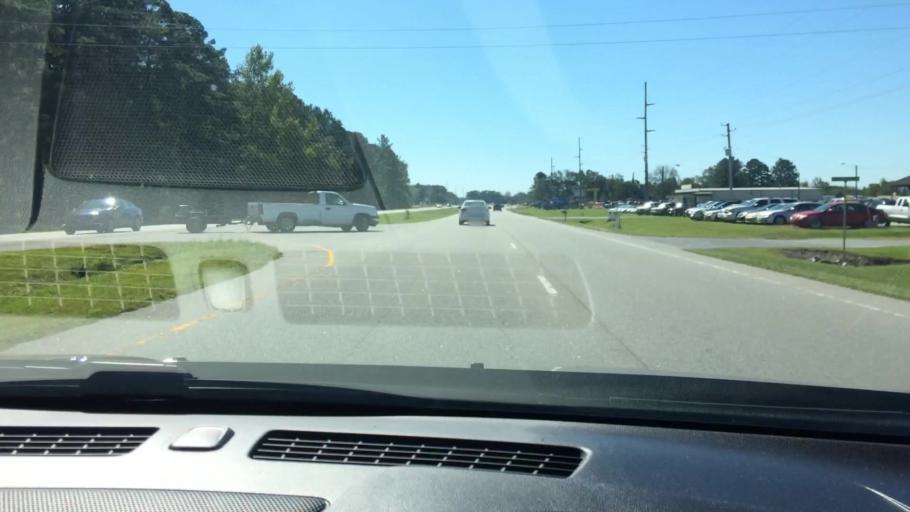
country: US
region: North Carolina
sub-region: Pitt County
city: Grifton
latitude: 35.4149
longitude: -77.4348
